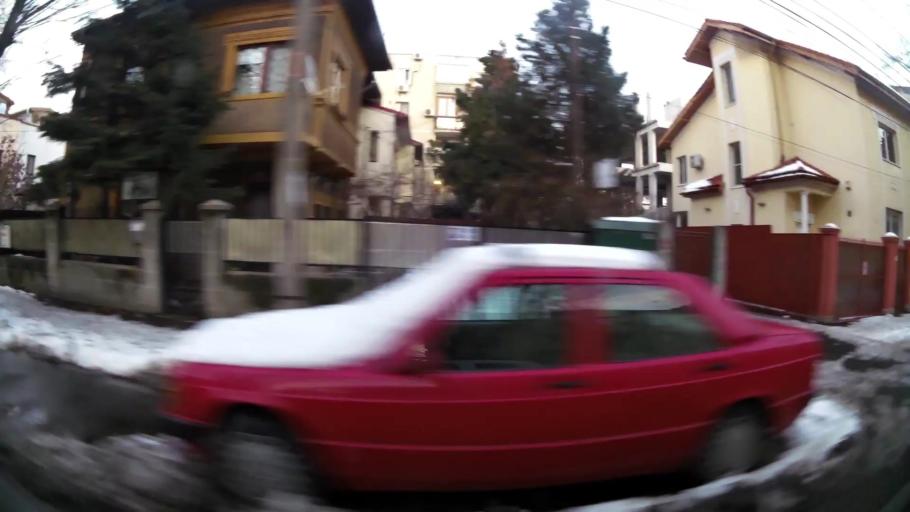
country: RO
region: Ilfov
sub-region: Comuna Fundeni-Dobroesti
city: Fundeni
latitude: 44.4374
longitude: 26.1418
